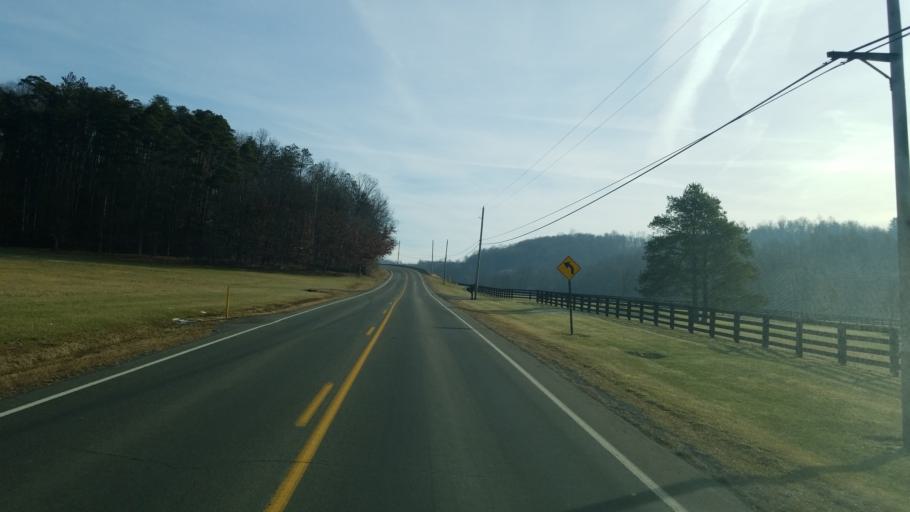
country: US
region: Pennsylvania
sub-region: Indiana County
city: Chevy Chase Heights
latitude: 40.7596
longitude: -79.1379
